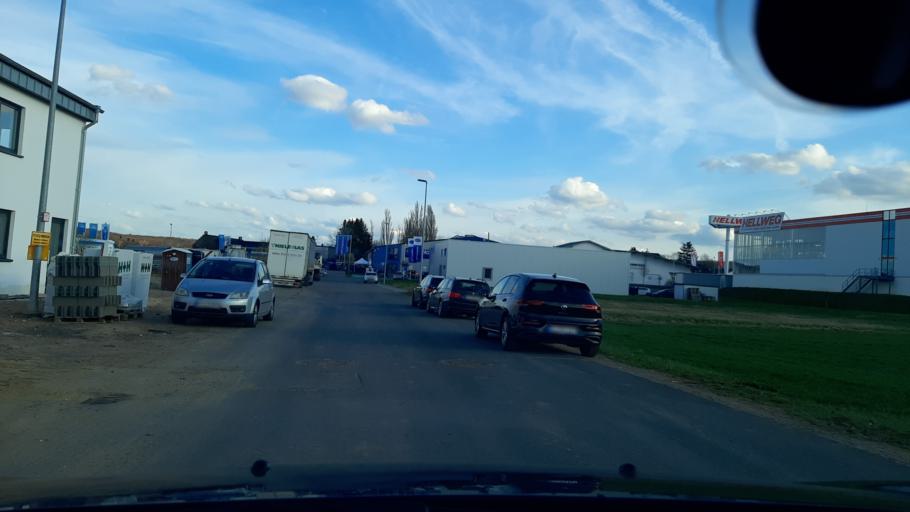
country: DE
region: North Rhine-Westphalia
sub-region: Regierungsbezirk Koln
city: Mechernich
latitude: 50.6199
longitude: 6.6493
